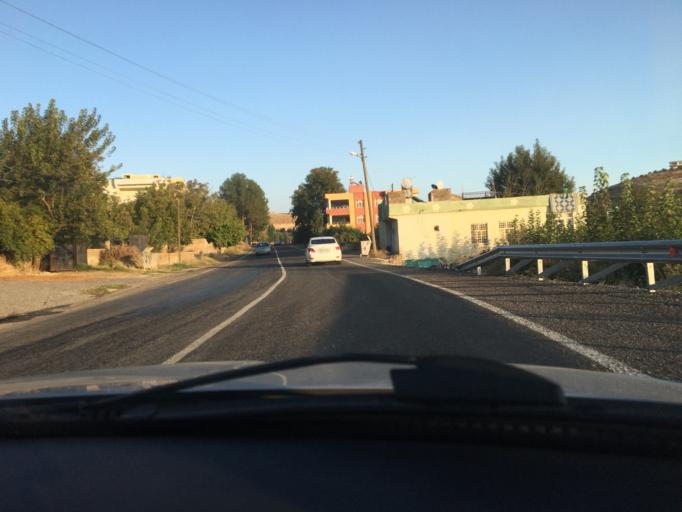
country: TR
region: Sanliurfa
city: Halfeti
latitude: 37.2088
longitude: 37.9652
